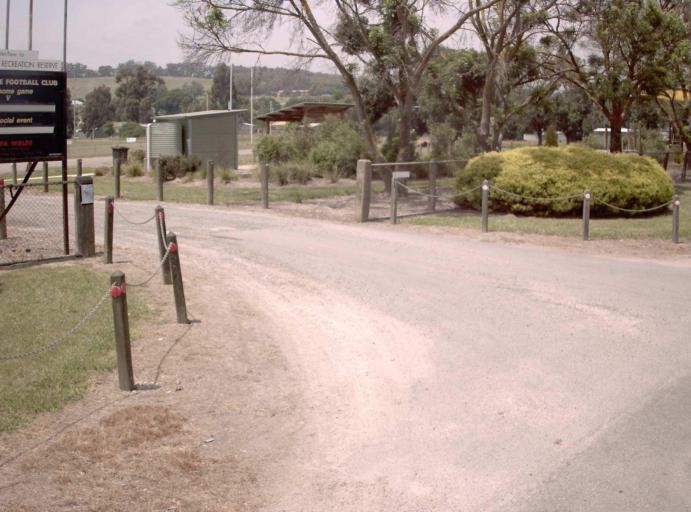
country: AU
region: Victoria
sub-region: Latrobe
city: Traralgon
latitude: -38.2922
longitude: 146.7007
